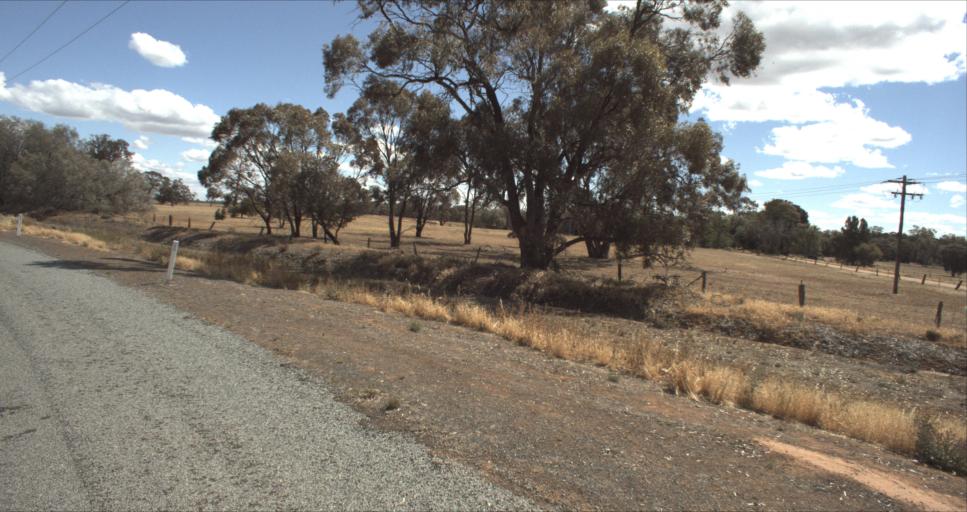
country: AU
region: New South Wales
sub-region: Leeton
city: Leeton
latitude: -34.5186
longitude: 146.2254
